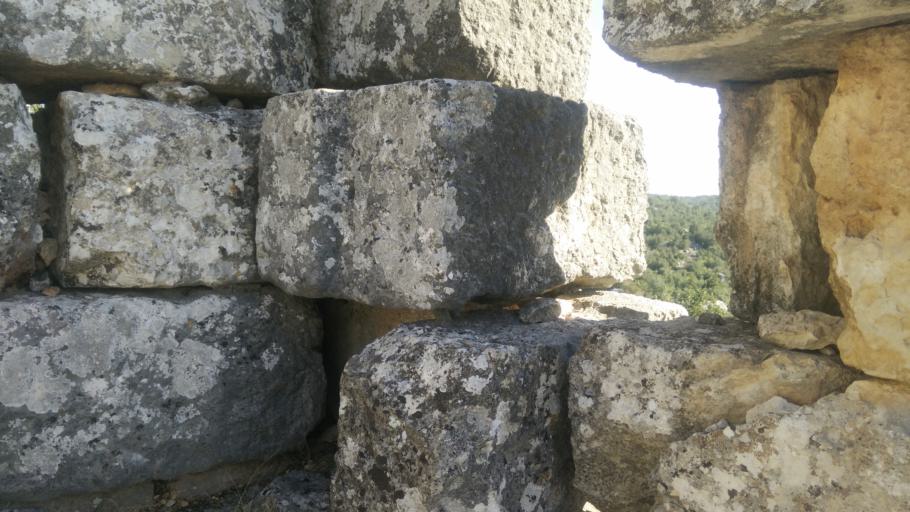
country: TR
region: Mersin
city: Kirobasi
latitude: 36.5839
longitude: 33.9660
